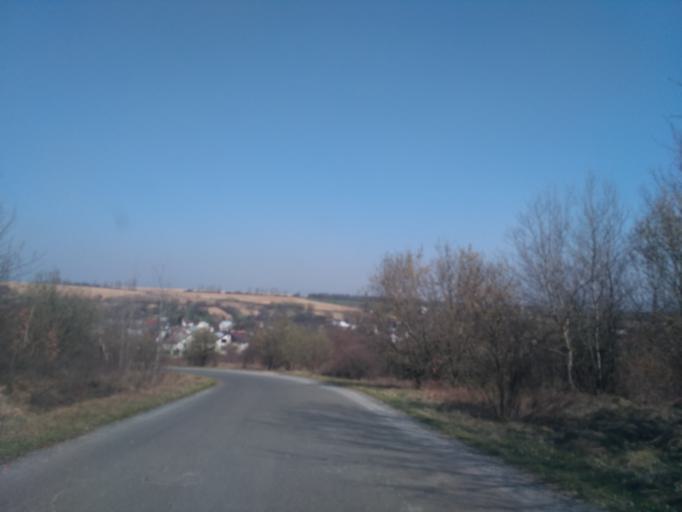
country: SK
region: Presovsky
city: Vranov nad Topl'ou
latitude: 48.8205
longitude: 21.6377
